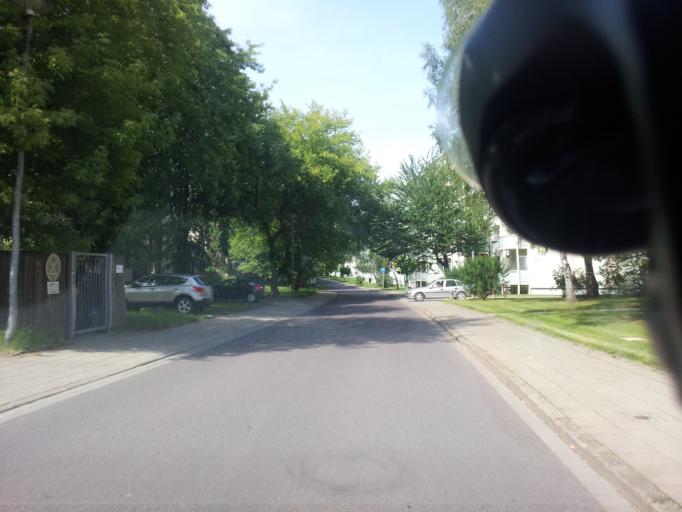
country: DE
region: Saxony-Anhalt
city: Quedlinburg
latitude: 51.7795
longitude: 11.1570
